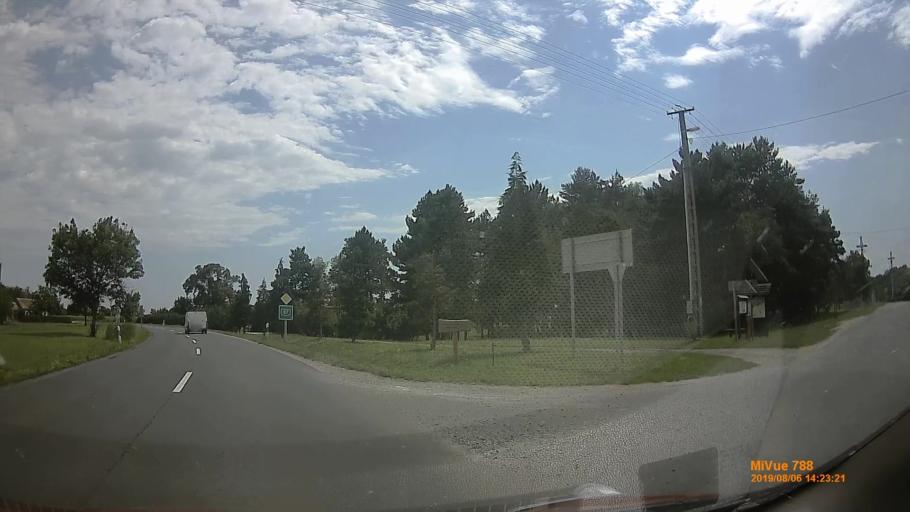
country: HU
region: Vas
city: Vasvar
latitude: 47.1547
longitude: 16.8039
